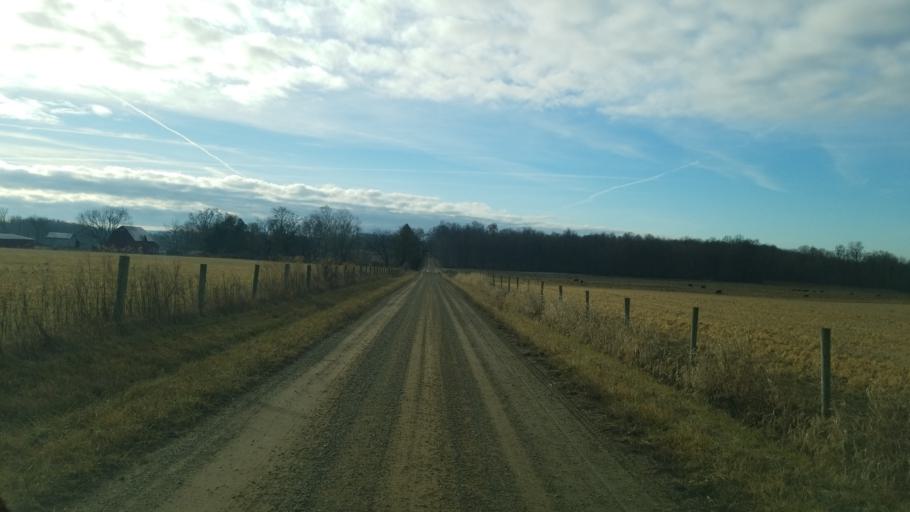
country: US
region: Ohio
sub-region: Knox County
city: Gambier
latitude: 40.3192
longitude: -82.3211
